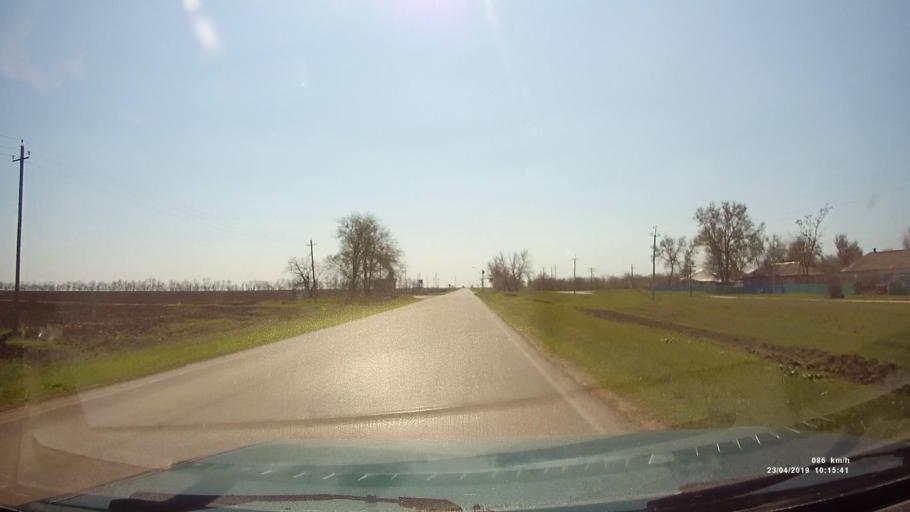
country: RU
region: Rostov
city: Sovetskoye
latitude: 46.6647
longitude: 42.3847
